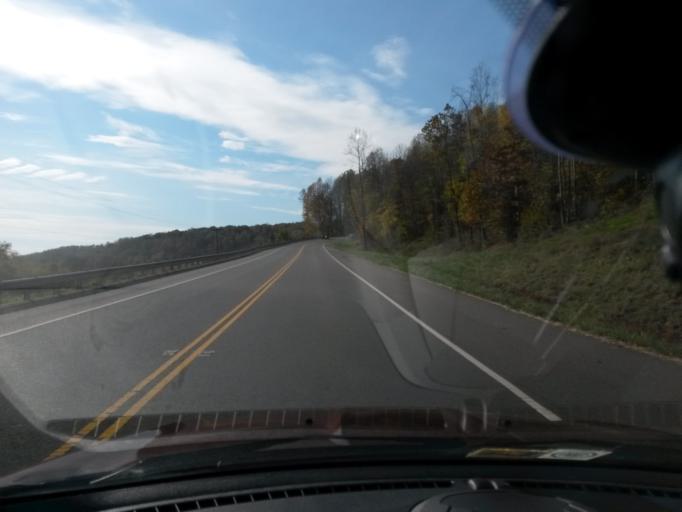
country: US
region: Virginia
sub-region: Franklin County
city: North Shore
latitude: 37.1238
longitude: -79.7829
